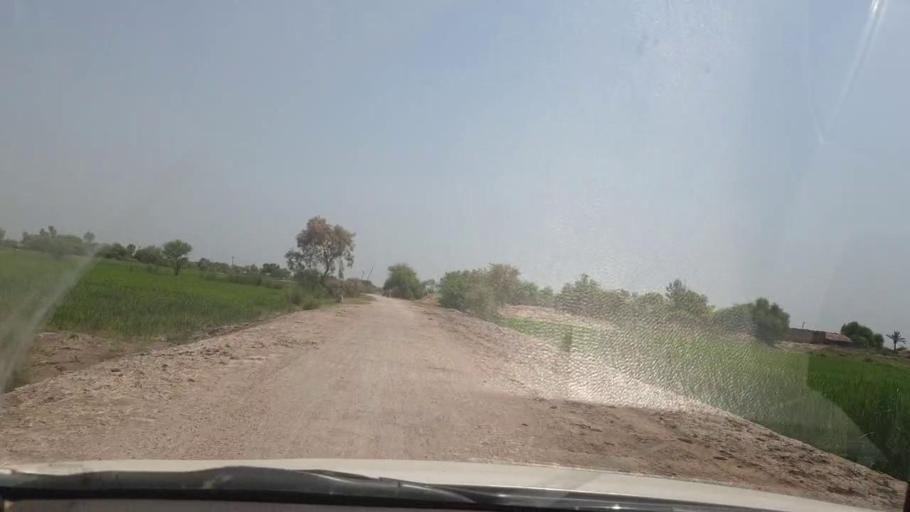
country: PK
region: Sindh
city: Lakhi
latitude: 27.8810
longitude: 68.7453
